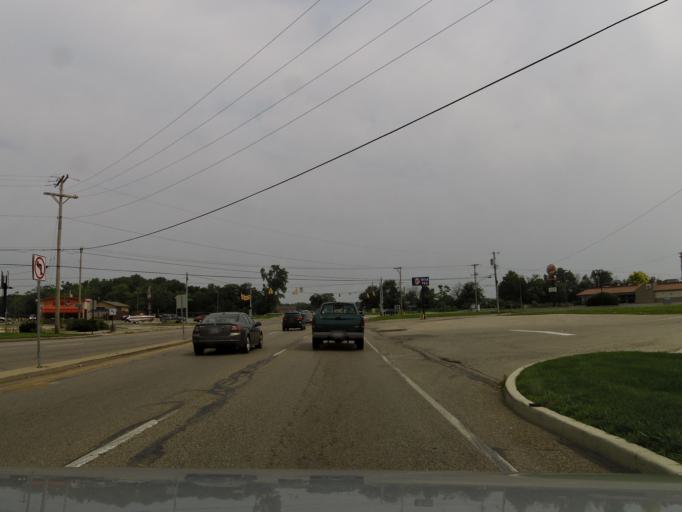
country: US
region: Ohio
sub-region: Montgomery County
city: Riverside
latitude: 39.7683
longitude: -84.1232
